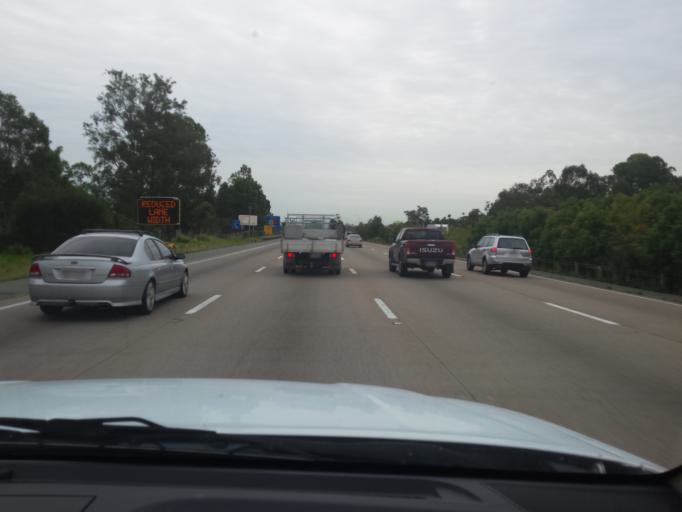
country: AU
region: Queensland
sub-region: Gold Coast
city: Oxenford
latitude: -27.8713
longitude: 153.3134
